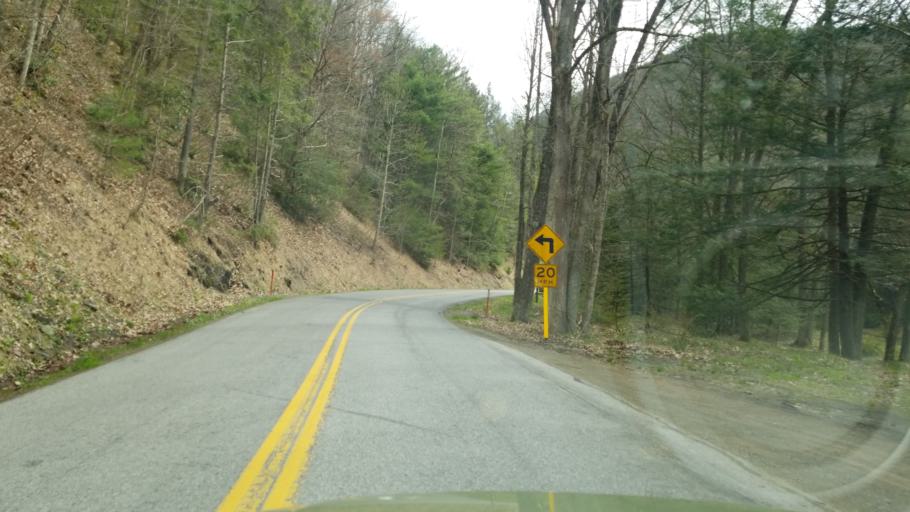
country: US
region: Pennsylvania
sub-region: Cameron County
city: Emporium
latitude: 41.2896
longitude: -78.1205
